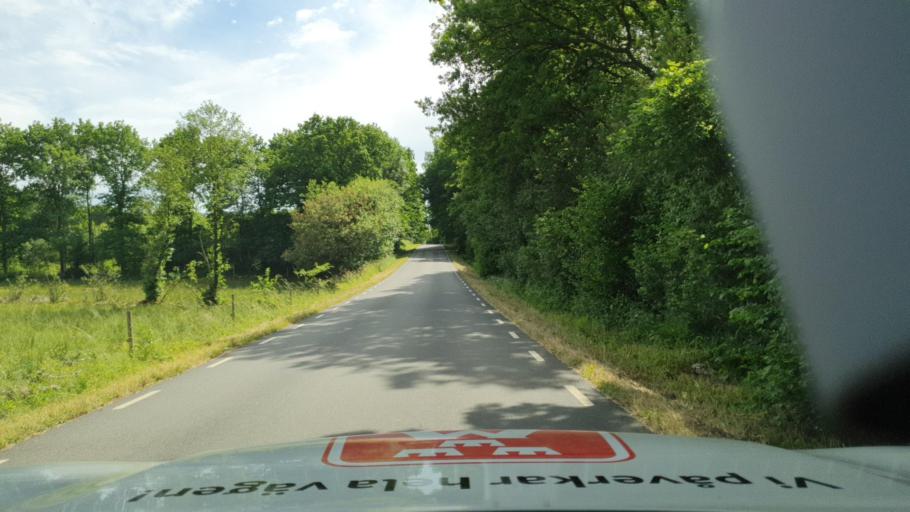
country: SE
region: Skane
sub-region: Tomelilla Kommun
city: Tomelilla
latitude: 55.6892
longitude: 13.9468
